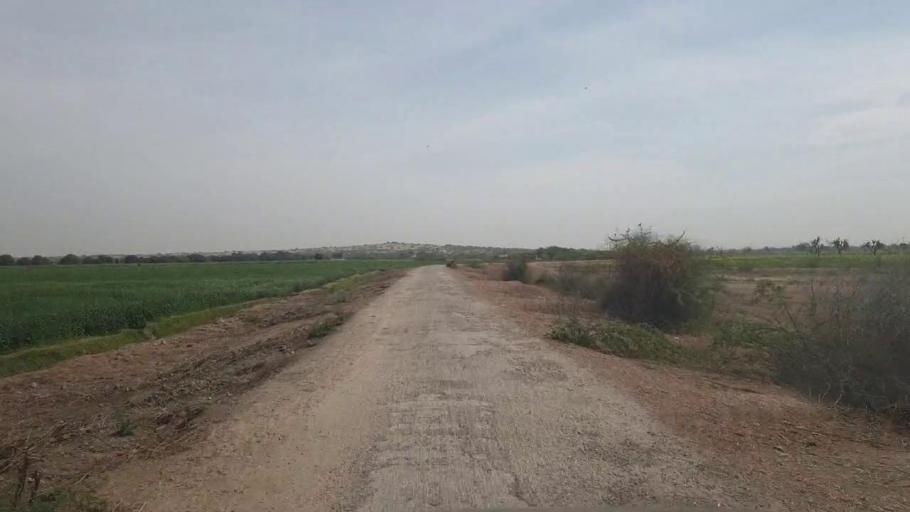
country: PK
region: Sindh
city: Umarkot
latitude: 25.2720
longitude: 69.6990
